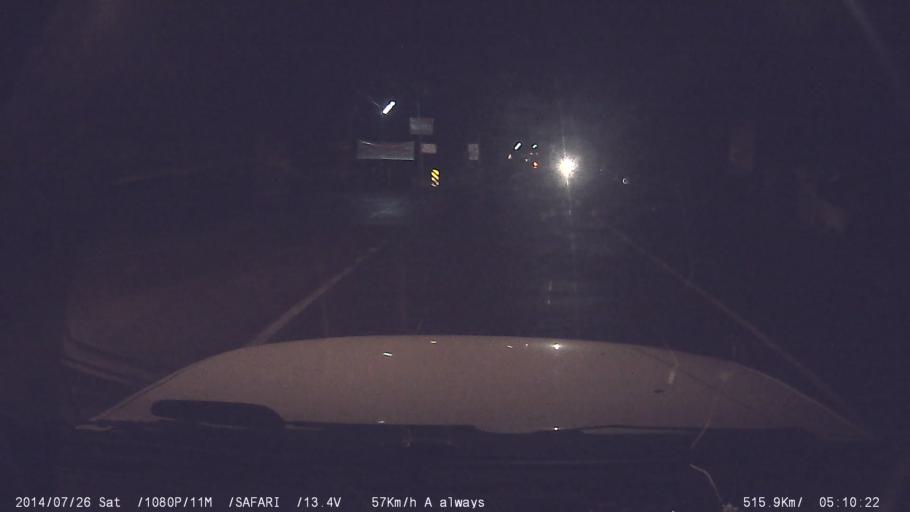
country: IN
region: Kerala
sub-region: Ernakulam
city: Perumbavoor
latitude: 10.0587
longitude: 76.5271
